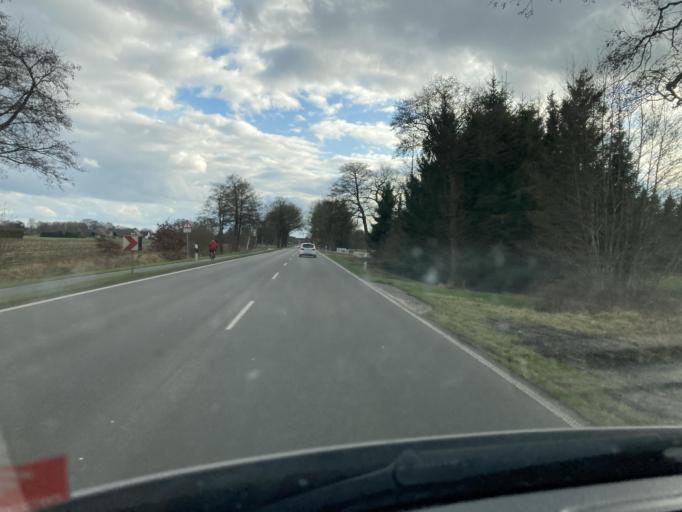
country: DE
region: Lower Saxony
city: Ostrhauderfehn
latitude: 53.1520
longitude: 7.5621
